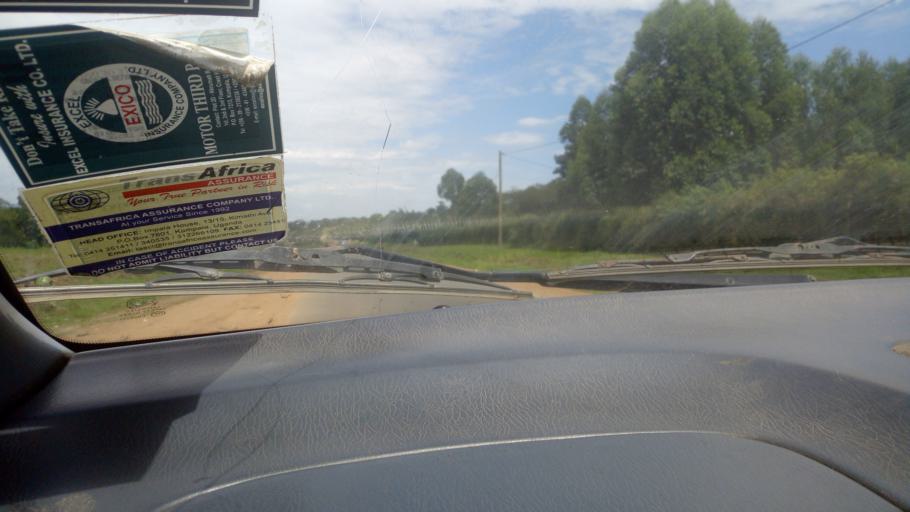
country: UG
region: Western Region
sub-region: Mbarara District
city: Bwizibwera
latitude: -0.4049
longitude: 30.5686
